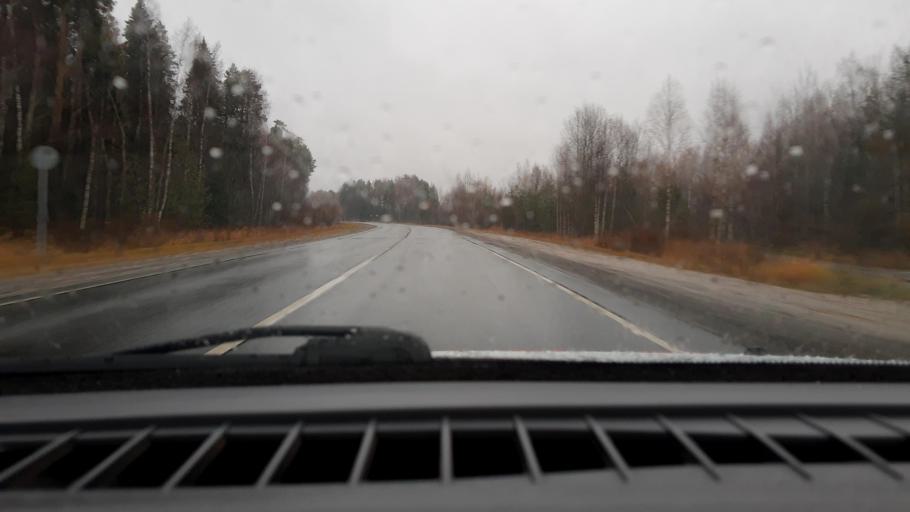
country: RU
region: Nizjnij Novgorod
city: Linda
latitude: 56.6433
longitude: 44.1117
